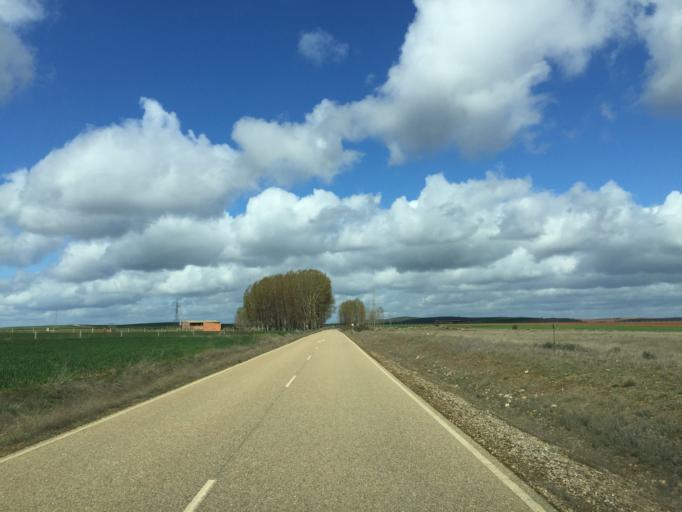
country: ES
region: Castille and Leon
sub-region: Provincia de Zamora
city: Palacios del Pan
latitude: 41.5788
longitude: -5.9268
